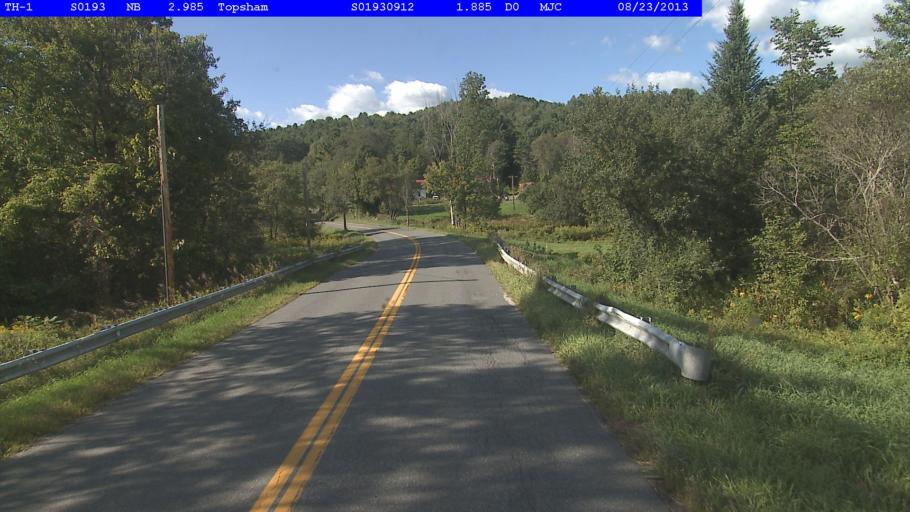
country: US
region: New Hampshire
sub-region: Grafton County
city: Haverhill
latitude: 44.0971
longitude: -72.2234
